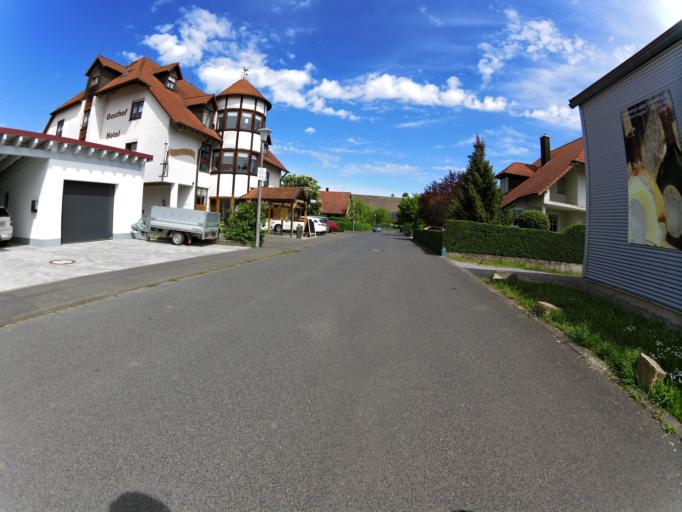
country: DE
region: Bavaria
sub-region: Regierungsbezirk Unterfranken
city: Nordheim
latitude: 49.8603
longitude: 10.1901
